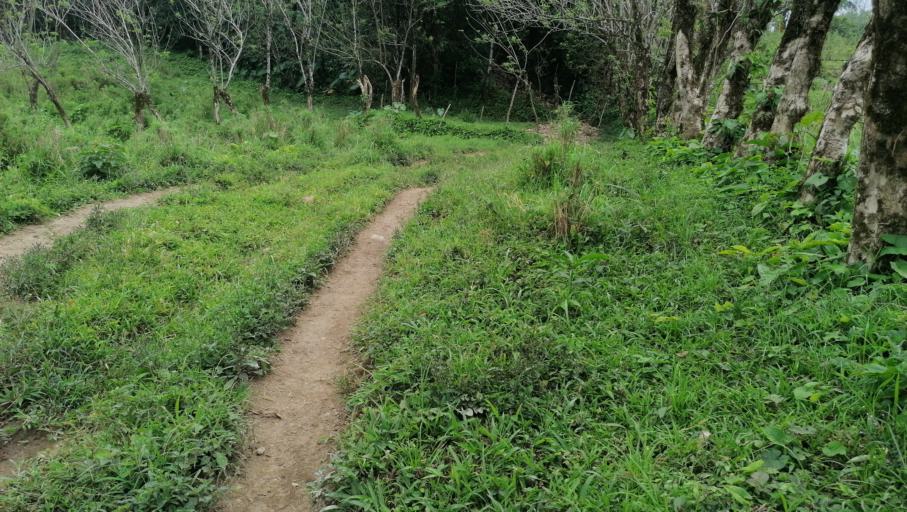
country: MX
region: Chiapas
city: Ocotepec
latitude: 17.2937
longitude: -93.2258
